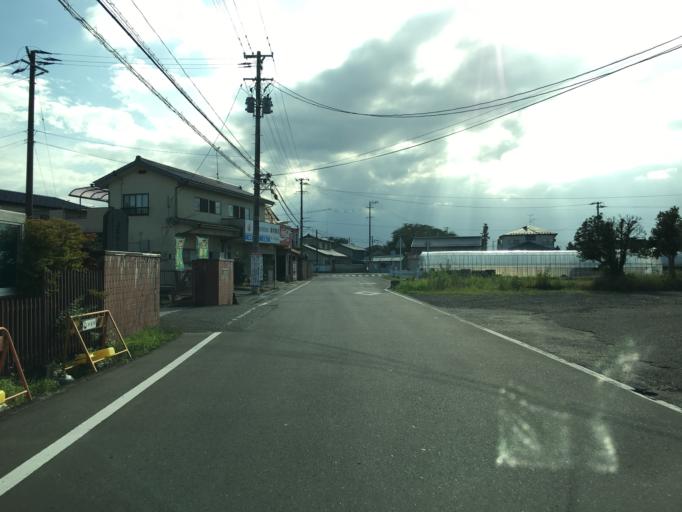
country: JP
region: Fukushima
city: Hobaramachi
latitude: 37.8258
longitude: 140.5731
